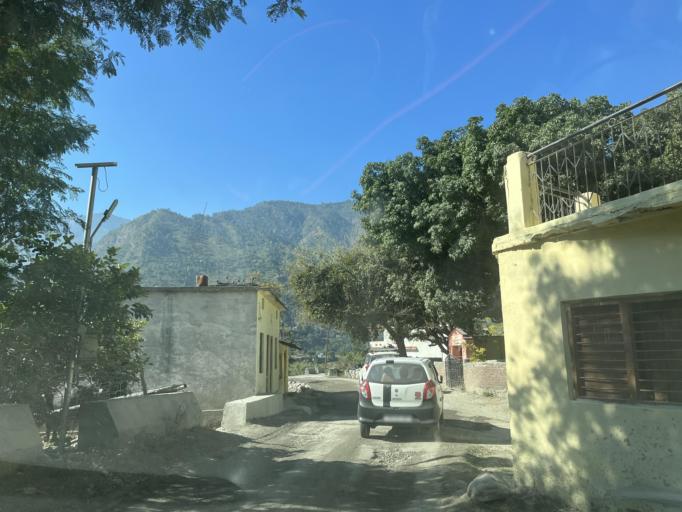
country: IN
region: Uttarakhand
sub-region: Naini Tal
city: Naini Tal
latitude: 29.5081
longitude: 79.4459
